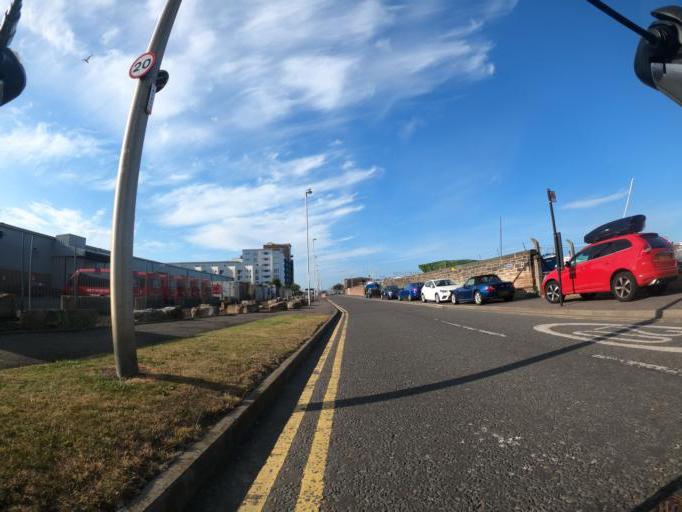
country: GB
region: Scotland
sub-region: Edinburgh
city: Edinburgh
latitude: 55.9820
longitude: -3.2238
